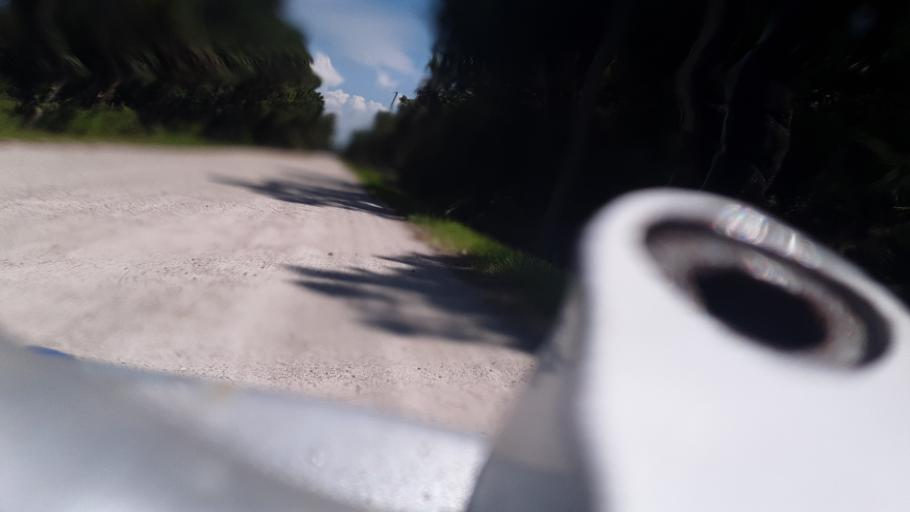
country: US
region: Florida
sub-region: Brevard County
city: Malabar
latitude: 27.9900
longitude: -80.5978
